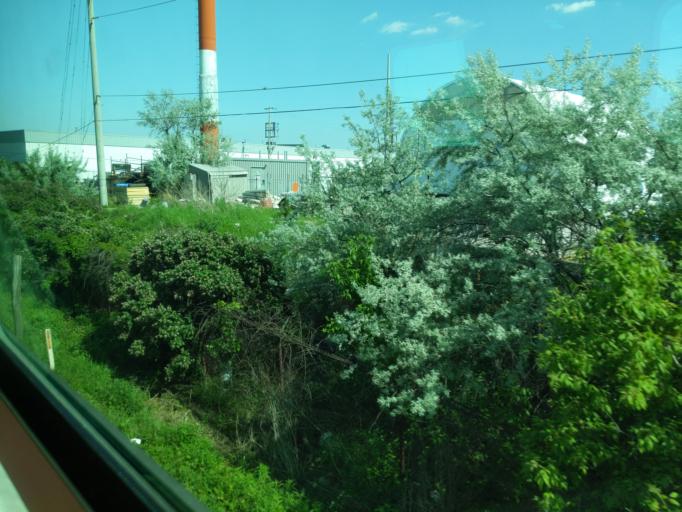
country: CA
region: Ontario
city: Etobicoke
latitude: 43.7049
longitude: -79.6320
